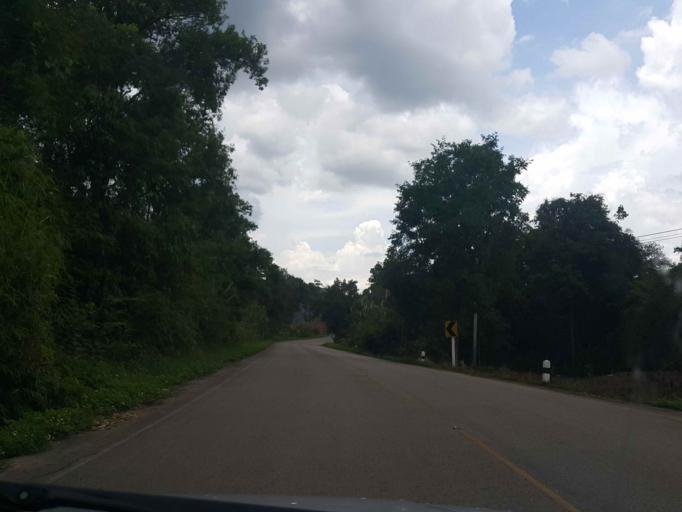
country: TH
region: Lampang
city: Ngao
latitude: 18.9373
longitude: 100.0800
